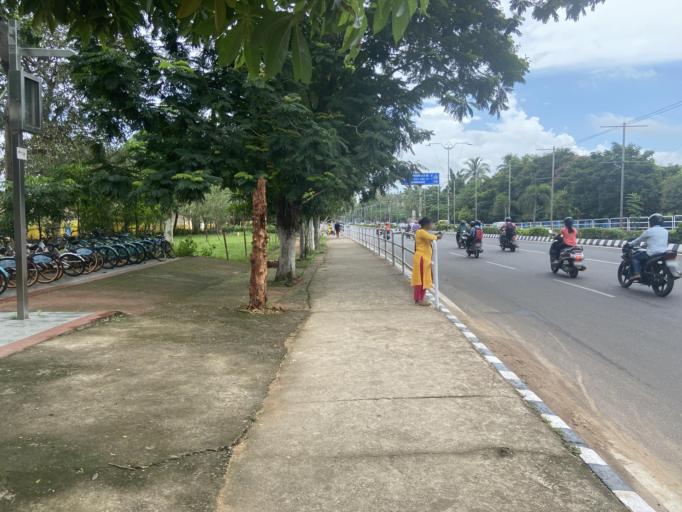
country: IN
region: Odisha
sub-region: Khordha
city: Bhubaneshwar
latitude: 20.2923
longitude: 85.8256
